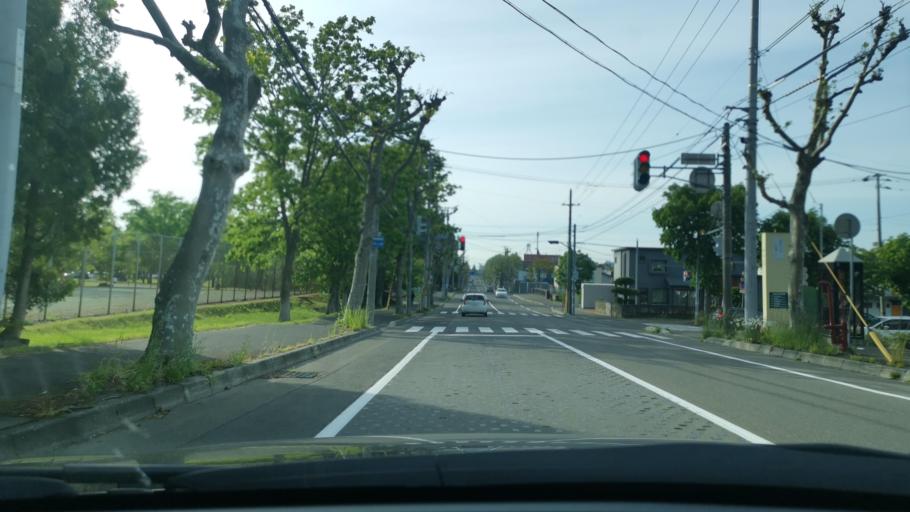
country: JP
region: Hokkaido
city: Iwamizawa
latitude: 43.1923
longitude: 141.7705
